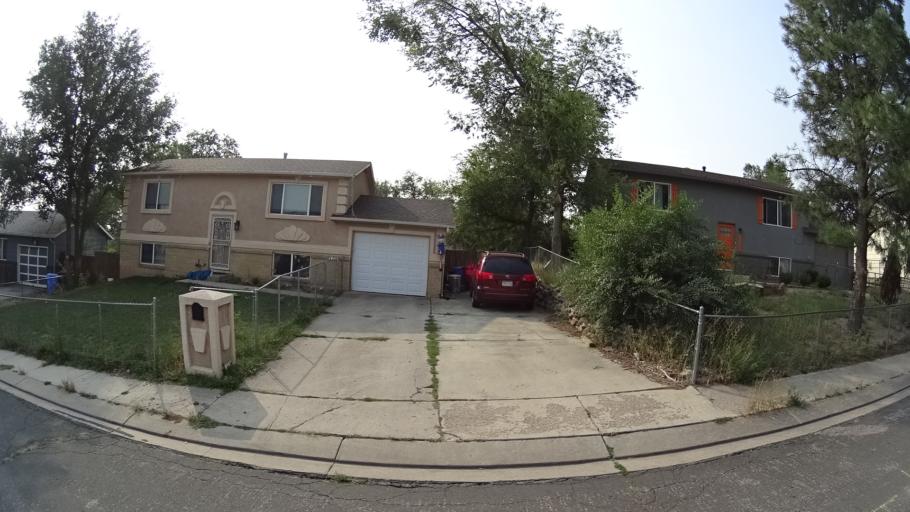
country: US
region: Colorado
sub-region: El Paso County
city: Stratmoor
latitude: 38.8051
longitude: -104.7653
